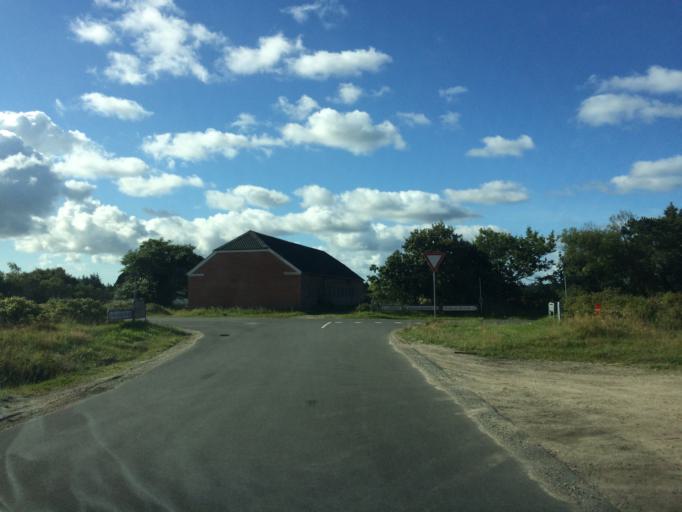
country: DK
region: South Denmark
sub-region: Varde Kommune
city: Oksbol
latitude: 55.6421
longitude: 8.1779
